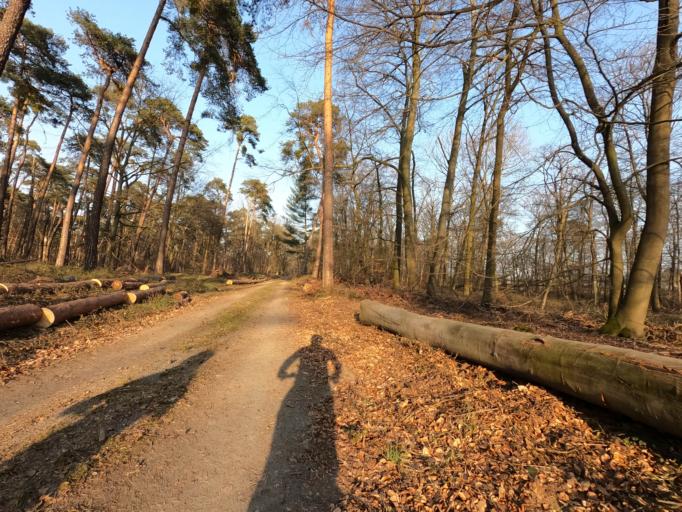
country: DE
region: Hesse
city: Raunheim
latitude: 50.0290
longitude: 8.4920
